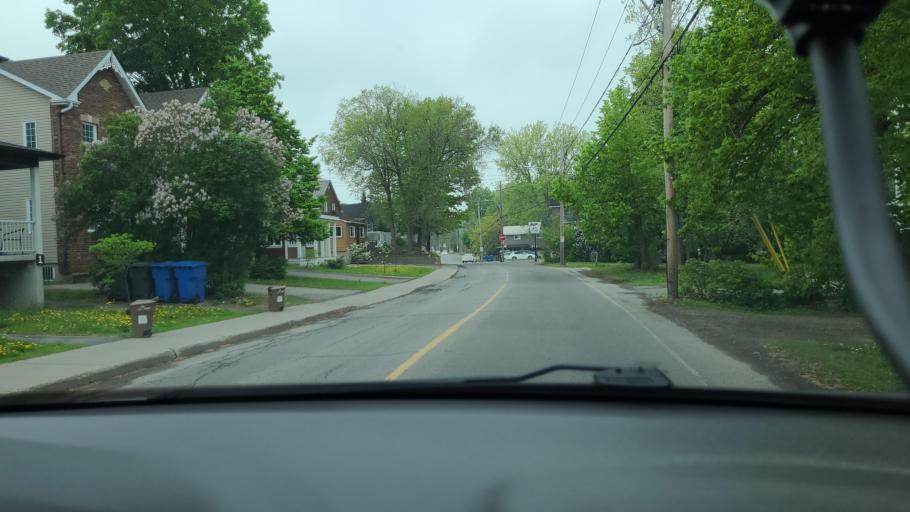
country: CA
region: Quebec
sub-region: Monteregie
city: L'Ile-Perrot
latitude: 45.3931
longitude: -73.9472
